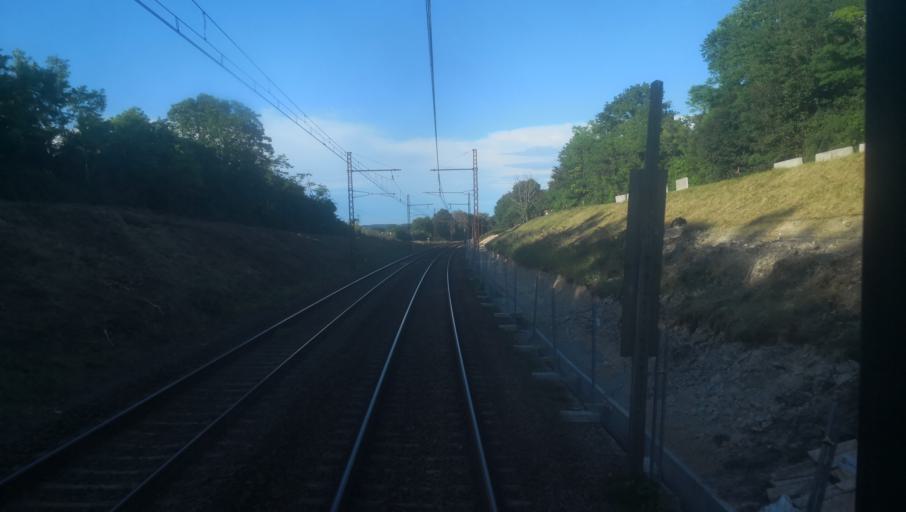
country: FR
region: Centre
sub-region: Departement du Cher
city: Vierzon
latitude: 47.1902
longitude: 2.0736
